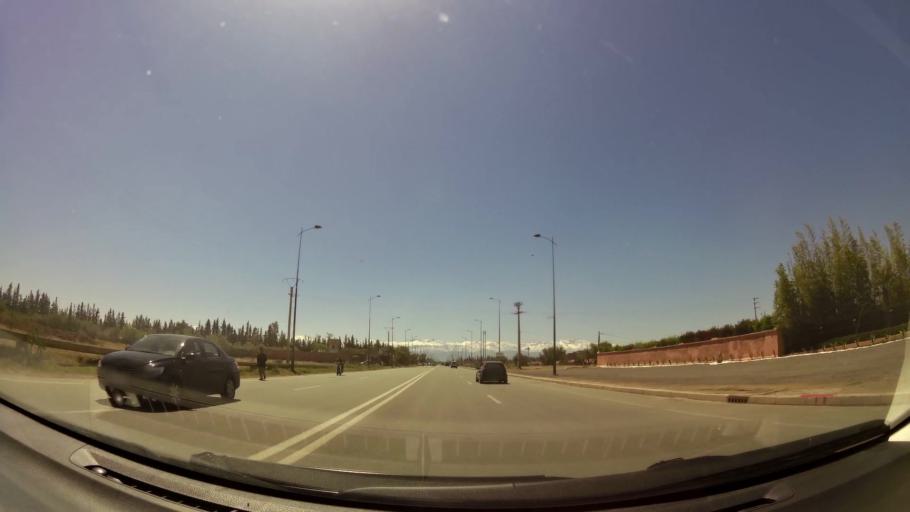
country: MA
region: Marrakech-Tensift-Al Haouz
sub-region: Marrakech
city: Marrakesh
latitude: 31.5571
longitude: -7.9766
